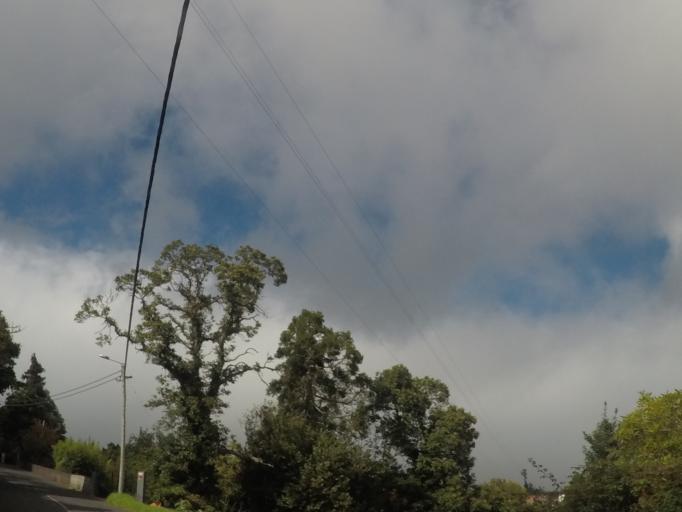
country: PT
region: Madeira
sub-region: Santa Cruz
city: Camacha
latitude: 32.6772
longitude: -16.8519
